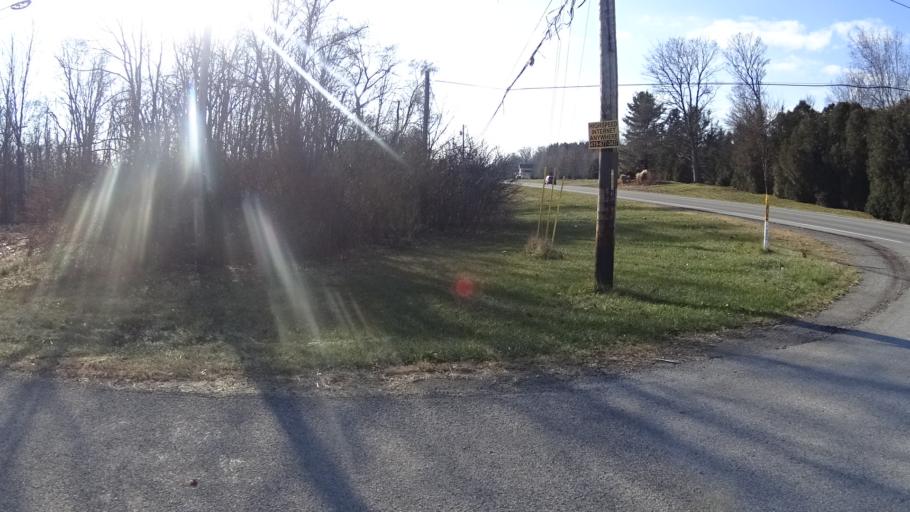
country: US
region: Ohio
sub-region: Lorain County
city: Wellington
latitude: 41.2235
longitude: -82.2187
